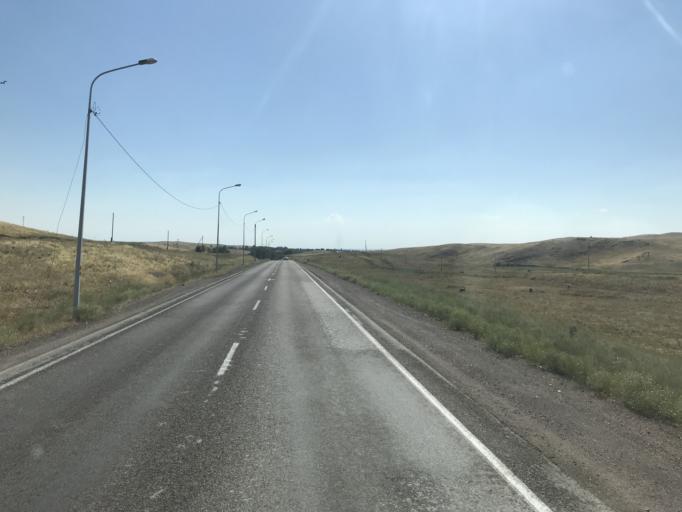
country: KZ
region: Zhambyl
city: Georgiyevka
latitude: 43.2442
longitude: 74.7833
